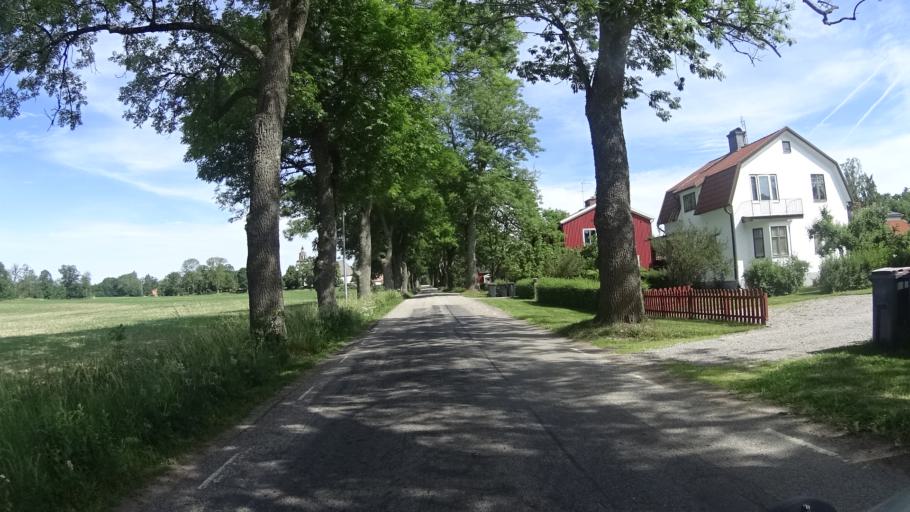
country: SE
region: Kalmar
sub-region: Vasterviks Kommun
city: Overum
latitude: 57.8933
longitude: 16.1695
